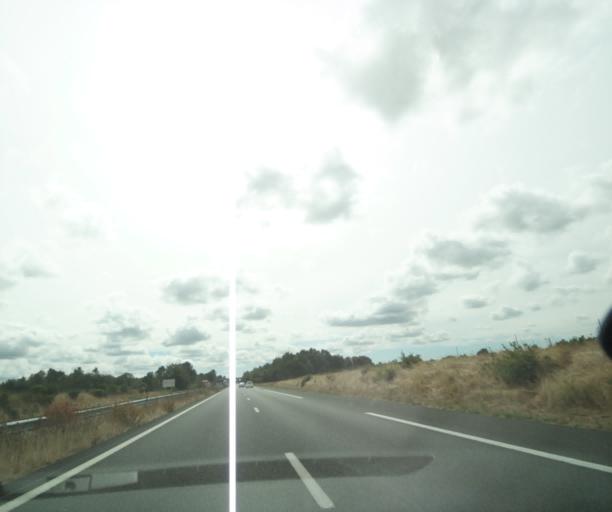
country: FR
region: Aquitaine
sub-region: Departement de la Gironde
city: Marcillac
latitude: 45.2439
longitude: -0.5349
